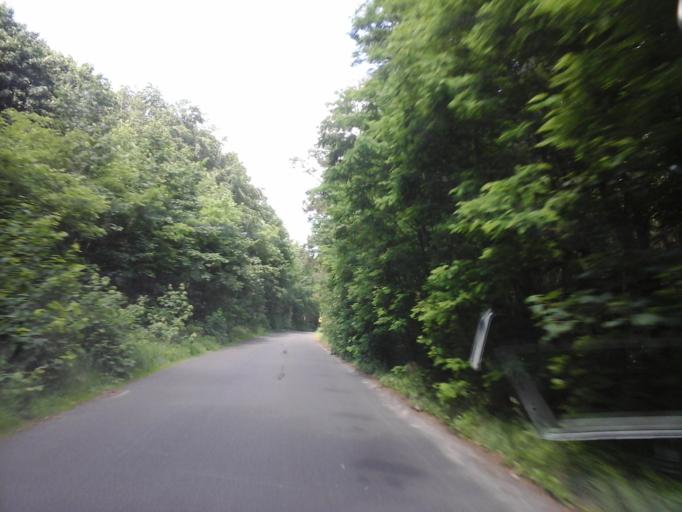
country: PL
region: Lubusz
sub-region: Powiat strzelecko-drezdenecki
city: Dobiegniew
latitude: 53.0822
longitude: 15.7769
